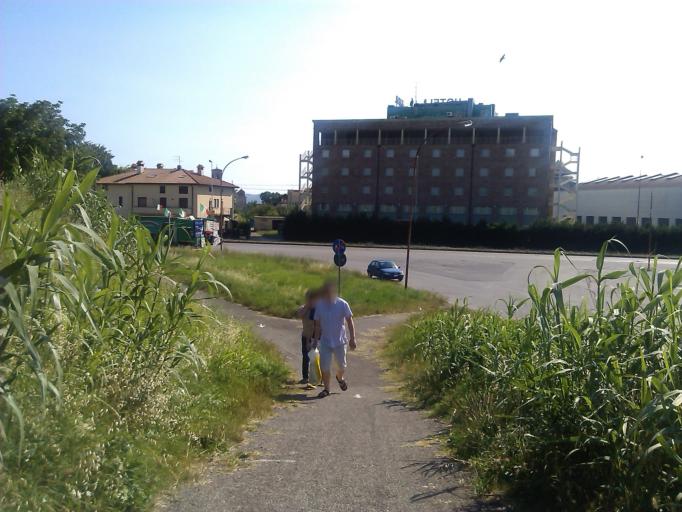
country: IT
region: Tuscany
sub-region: Province of Florence
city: Campi Bisenzio
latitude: 43.8575
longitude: 11.1233
